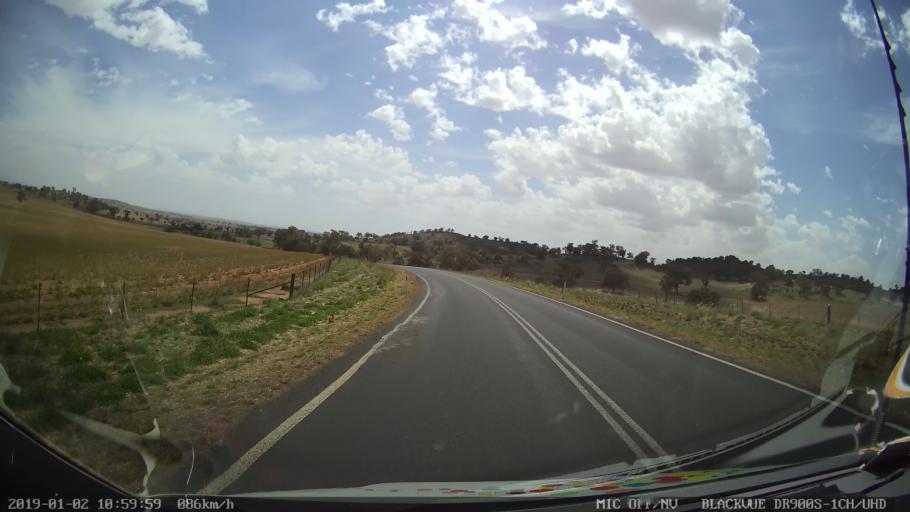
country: AU
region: New South Wales
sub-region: Cootamundra
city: Cootamundra
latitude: -34.6098
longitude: 148.3118
